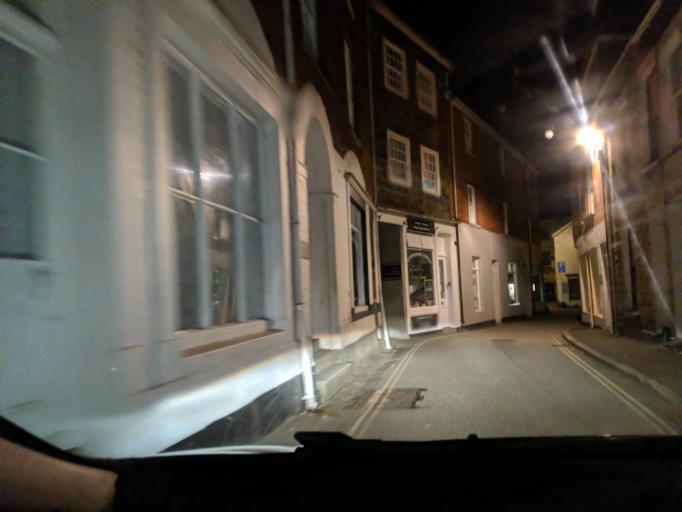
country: GB
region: England
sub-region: Cornwall
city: Mevagissey
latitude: 50.2708
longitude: -4.7874
